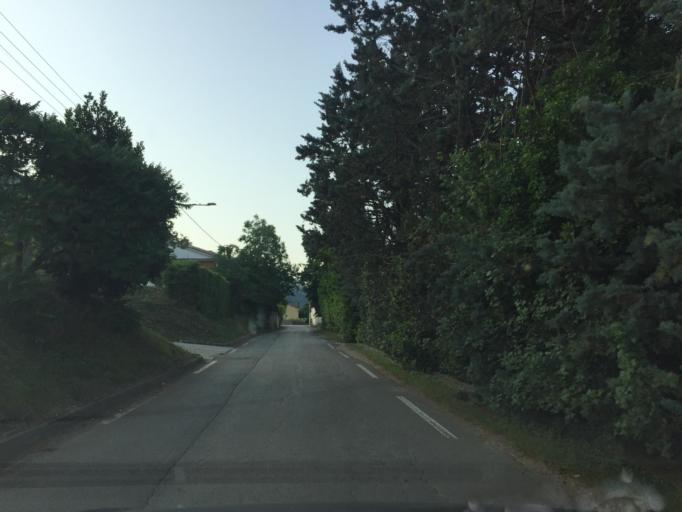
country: IT
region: Friuli Venezia Giulia
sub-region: Provincia di Trieste
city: Dolina
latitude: 45.5745
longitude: 13.8535
